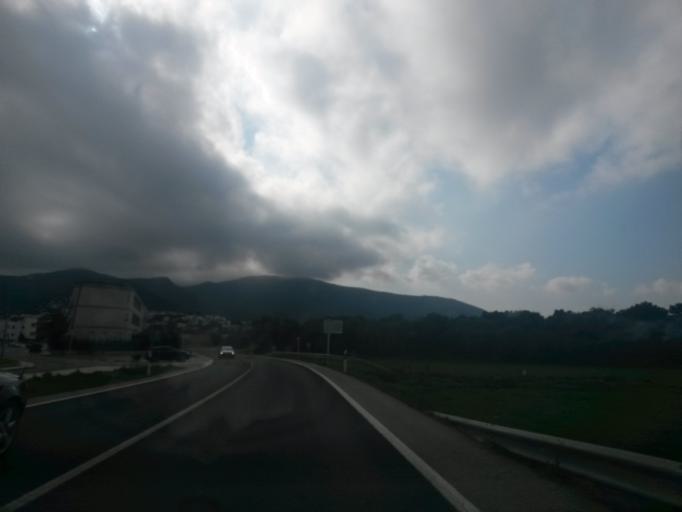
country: ES
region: Catalonia
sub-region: Provincia de Girona
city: Llanca
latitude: 42.3747
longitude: 3.1562
